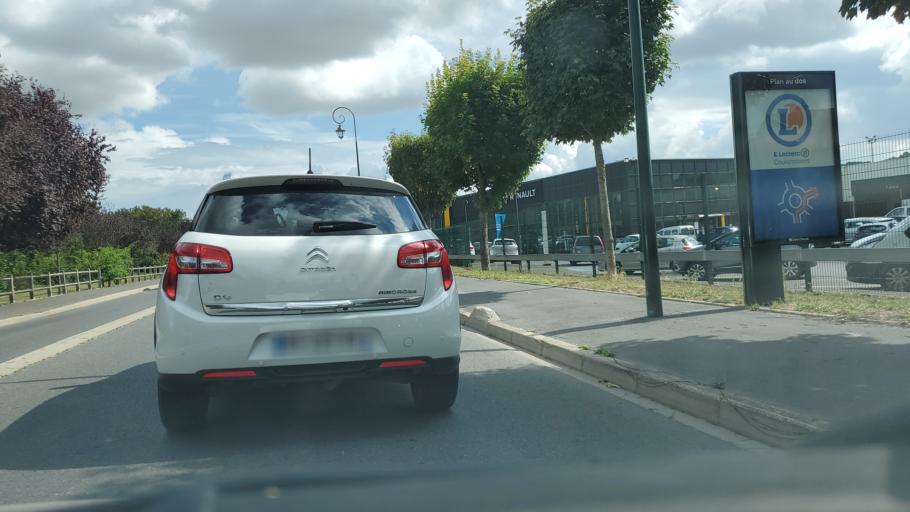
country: FR
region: Ile-de-France
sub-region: Departement de Seine-et-Marne
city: Coulommiers
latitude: 48.8103
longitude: 3.0799
